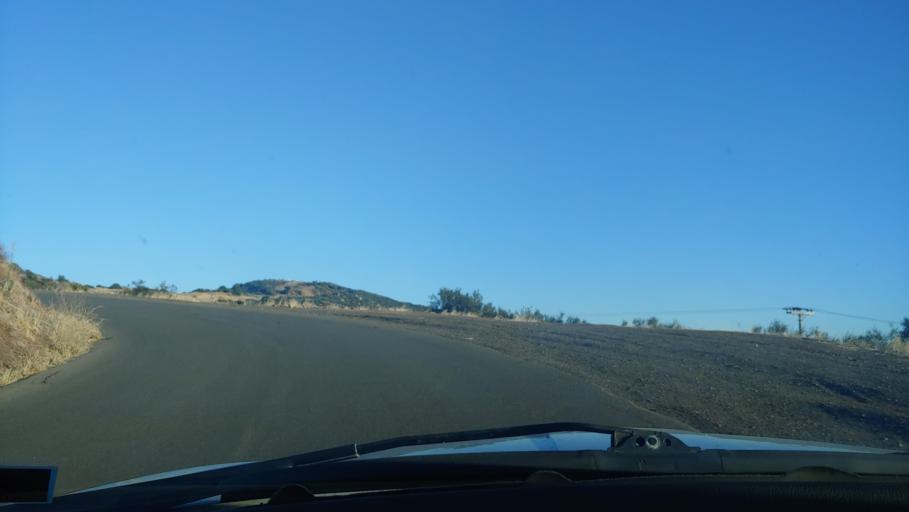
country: US
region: California
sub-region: Santa Barbara County
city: Goleta
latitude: 34.5187
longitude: -119.7870
